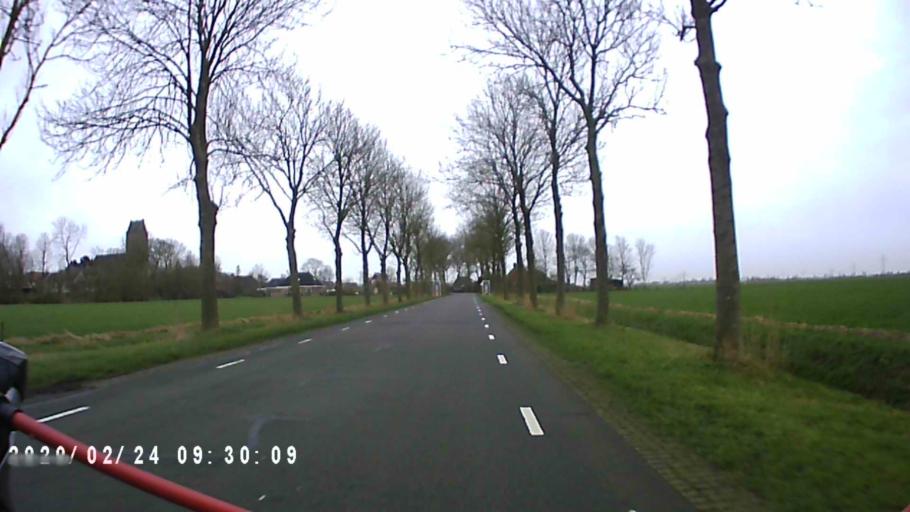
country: NL
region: Groningen
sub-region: Gemeente Winsum
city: Winsum
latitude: 53.3061
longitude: 6.4883
